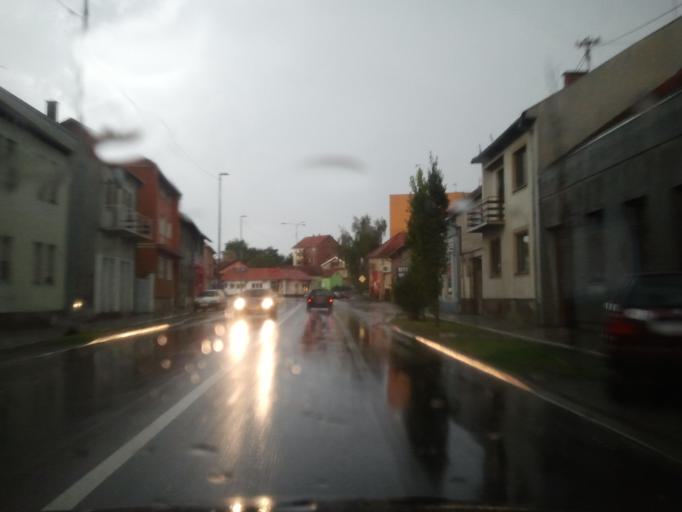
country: HR
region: Vukovarsko-Srijemska
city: Vukovar
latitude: 45.3449
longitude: 19.0082
